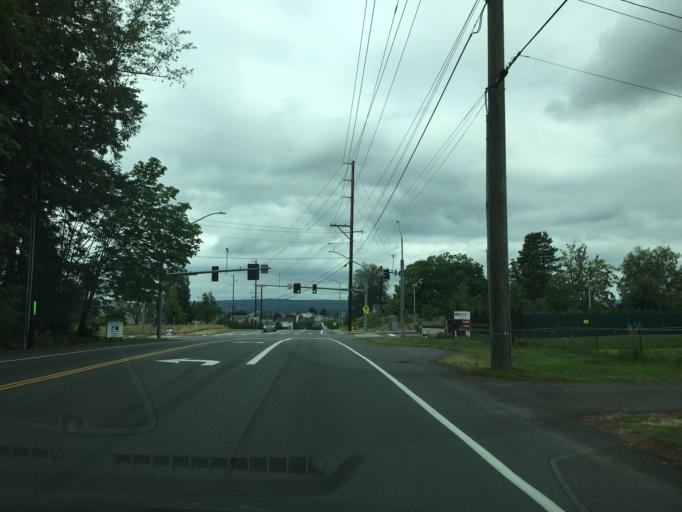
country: US
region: Washington
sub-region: Snohomish County
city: Sisco Heights
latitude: 48.0721
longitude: -122.1181
